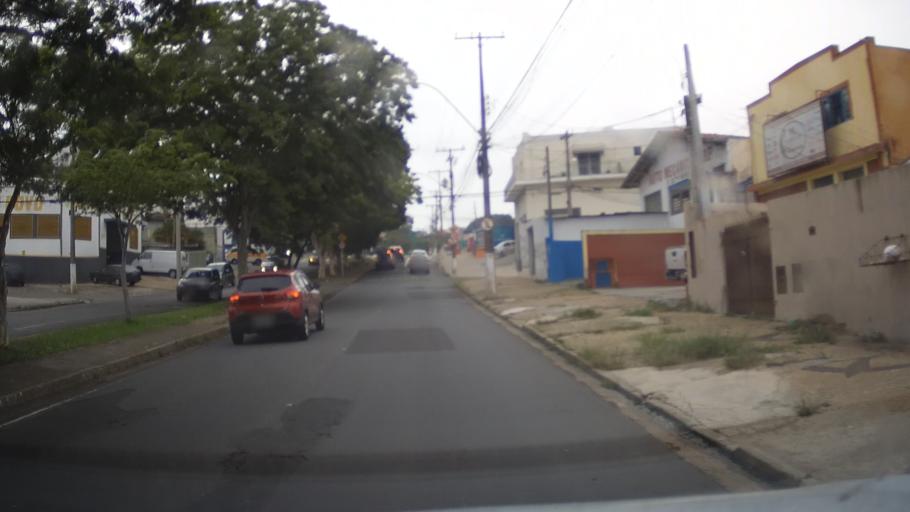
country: BR
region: Sao Paulo
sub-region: Campinas
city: Campinas
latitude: -22.9312
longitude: -47.0389
